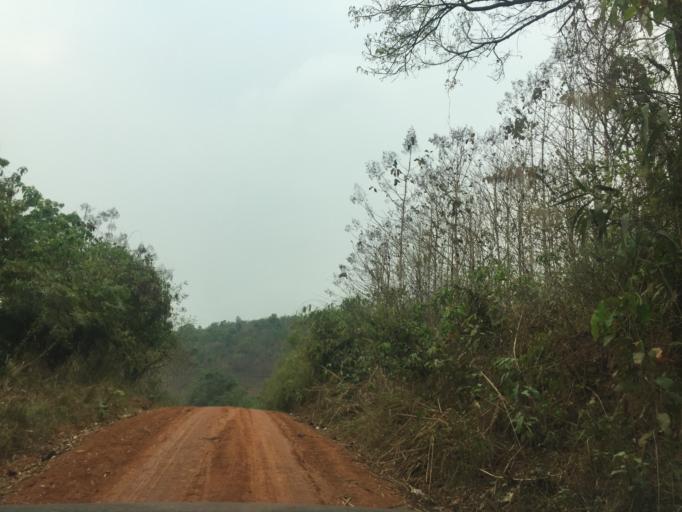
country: TH
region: Nan
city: Bo Kluea
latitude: 18.8527
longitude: 101.4180
